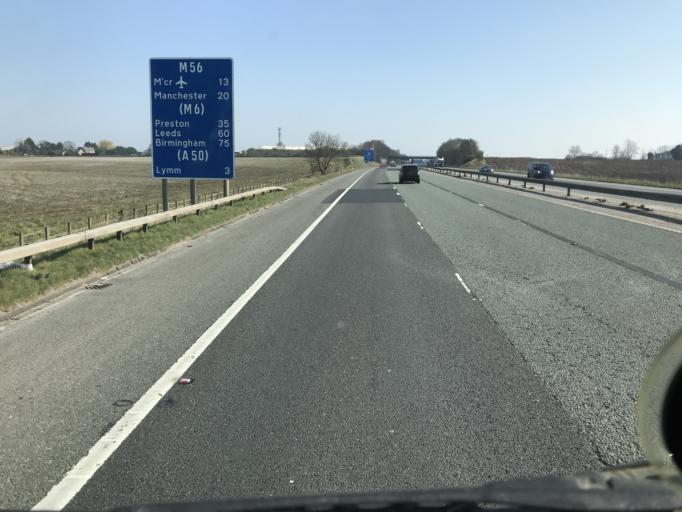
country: GB
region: England
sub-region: Warrington
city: Appleton Thorn
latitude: 53.3434
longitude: -2.5426
